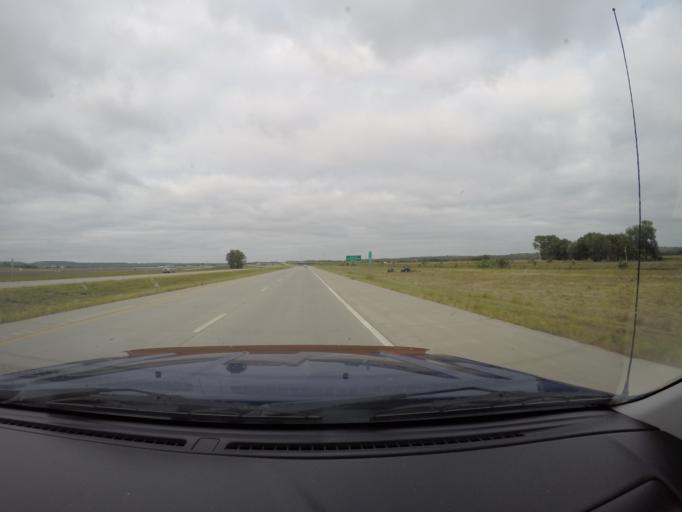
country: US
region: Kansas
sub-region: Riley County
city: Ogden
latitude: 39.1252
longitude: -96.6831
